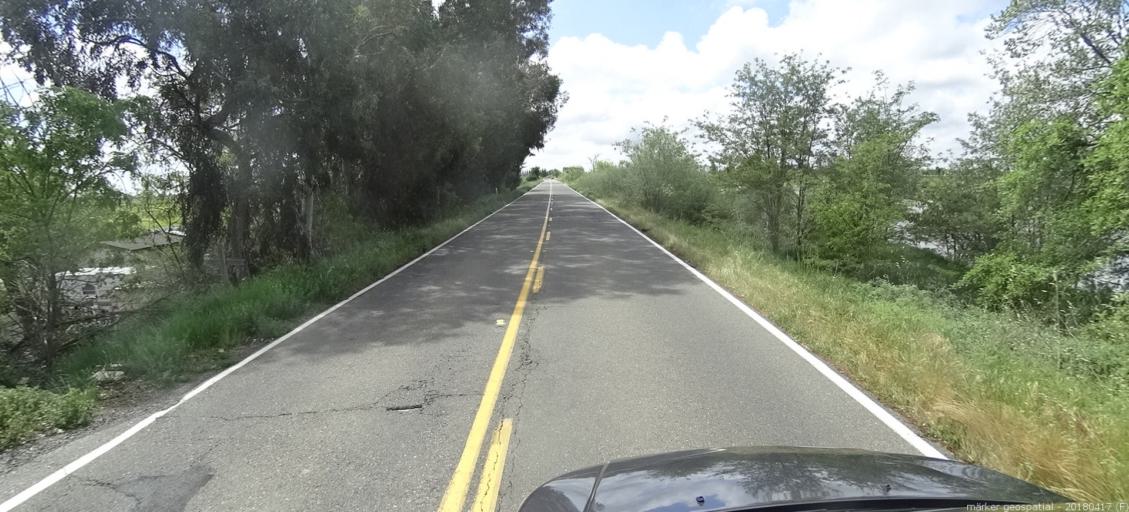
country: US
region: California
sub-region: Sacramento County
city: Walnut Grove
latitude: 38.2154
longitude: -121.5569
